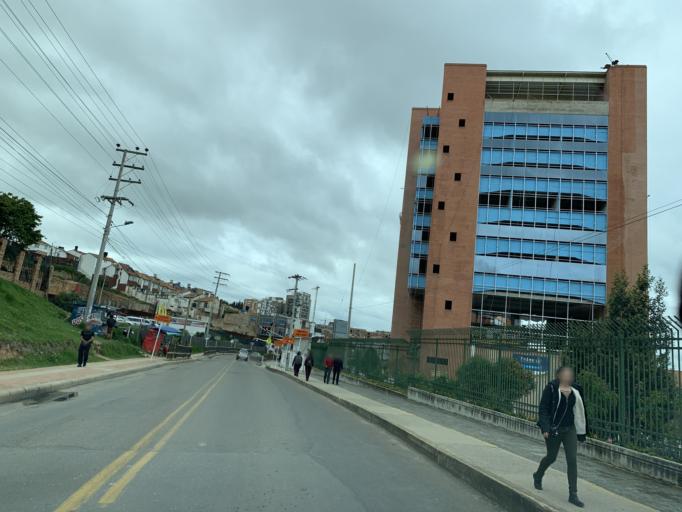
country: CO
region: Boyaca
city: Tunja
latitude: 5.5686
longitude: -73.3376
